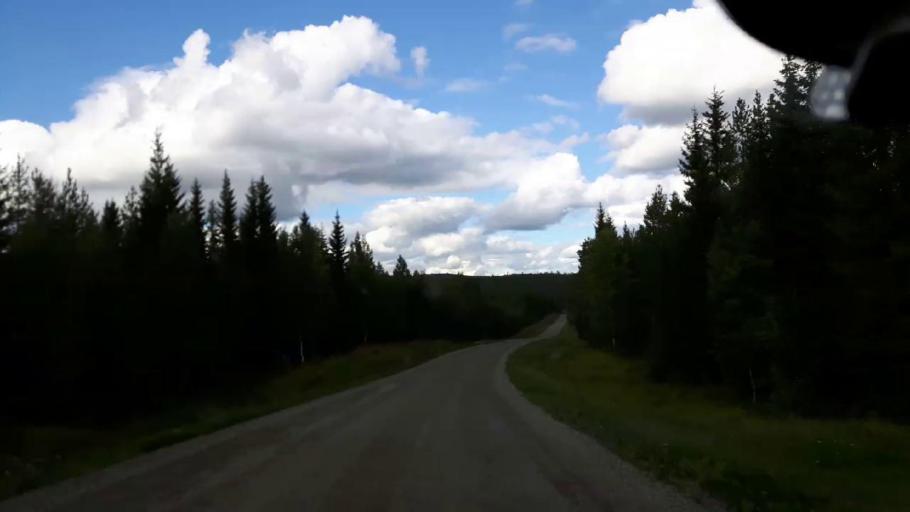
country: SE
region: Jaemtland
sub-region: Stroemsunds Kommun
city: Stroemsund
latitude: 63.4086
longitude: 15.5622
